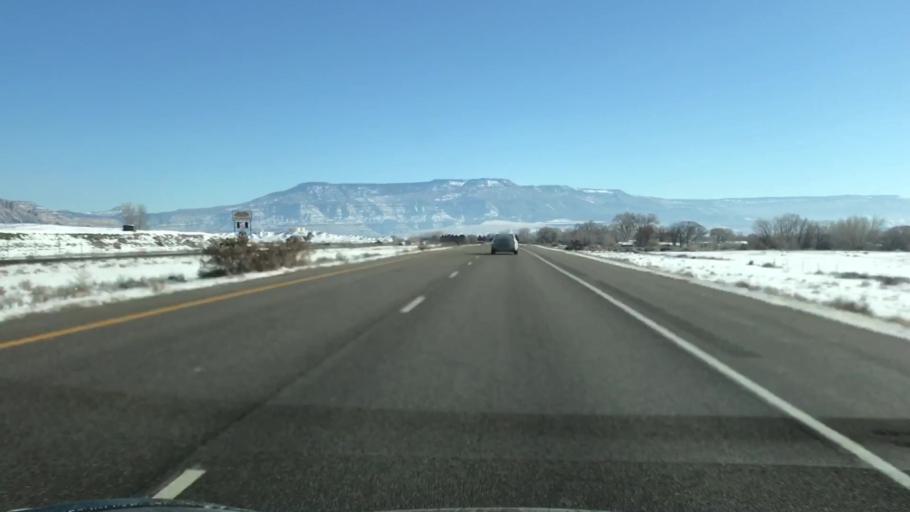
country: US
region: Colorado
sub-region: Mesa County
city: Fruitvale
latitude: 39.1070
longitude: -108.4938
